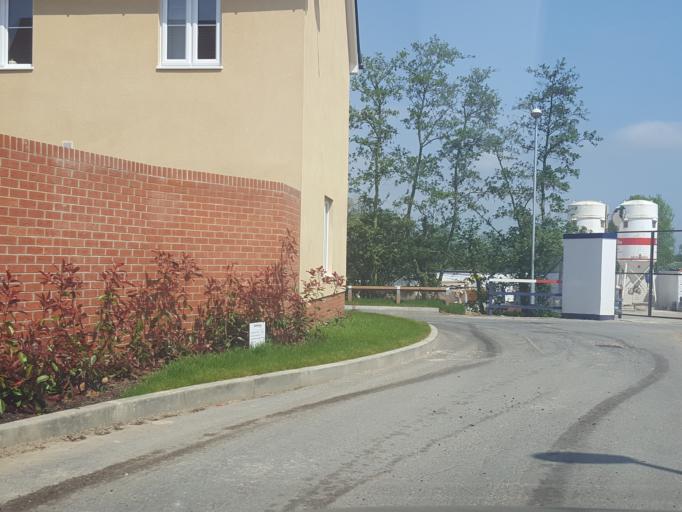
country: GB
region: England
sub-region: Essex
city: Colchester
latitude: 51.9169
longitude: 0.9328
